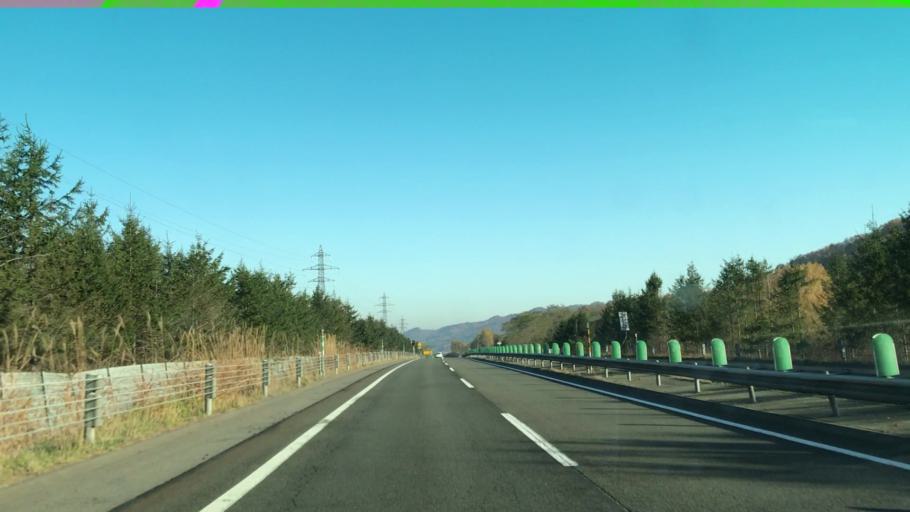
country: JP
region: Hokkaido
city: Sunagawa
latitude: 43.4245
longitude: 141.9119
